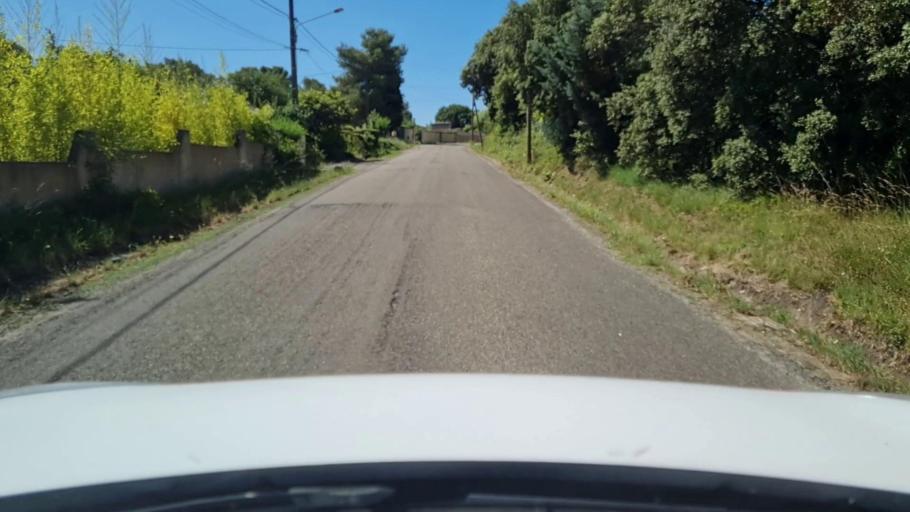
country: FR
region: Languedoc-Roussillon
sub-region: Departement du Gard
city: Villevieille
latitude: 43.7751
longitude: 4.1222
